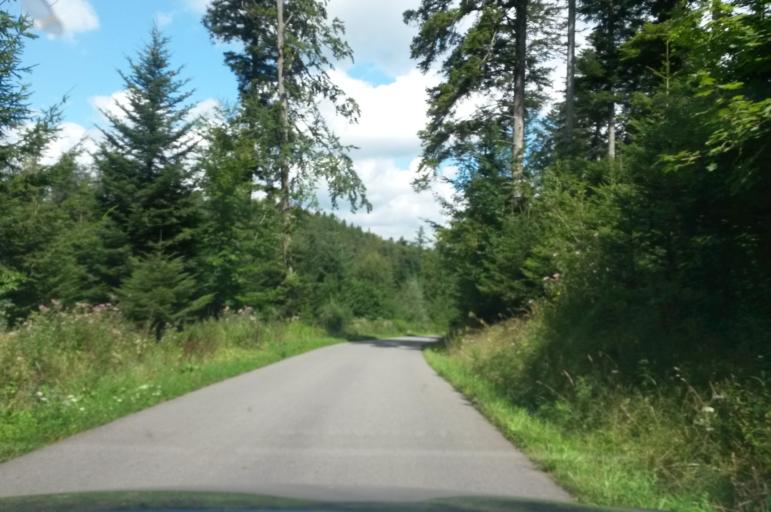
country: DE
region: Baden-Wuerttemberg
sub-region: Karlsruhe Region
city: Bad Herrenalb
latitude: 48.8415
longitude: 8.4602
